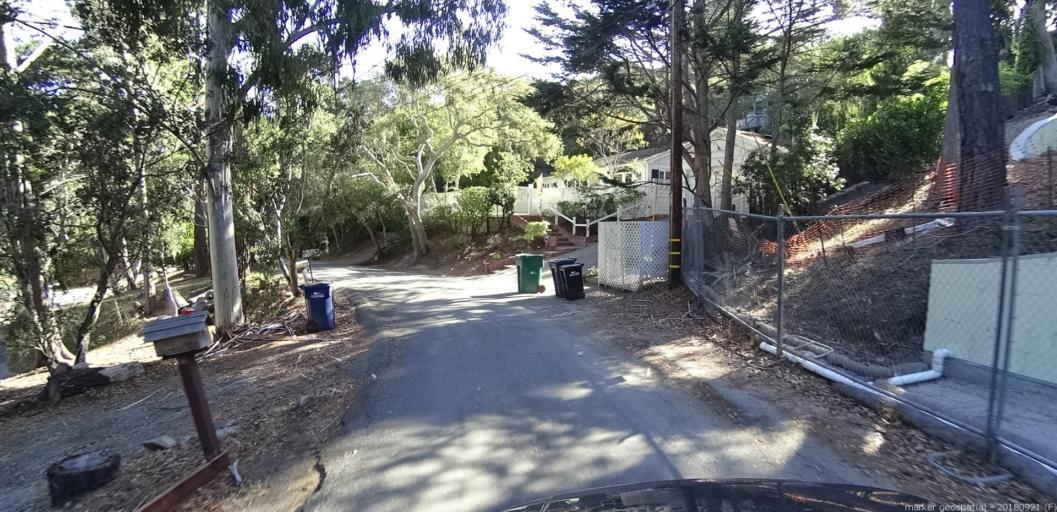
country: US
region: California
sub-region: Monterey County
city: Carmel-by-the-Sea
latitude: 36.5647
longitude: -121.9232
